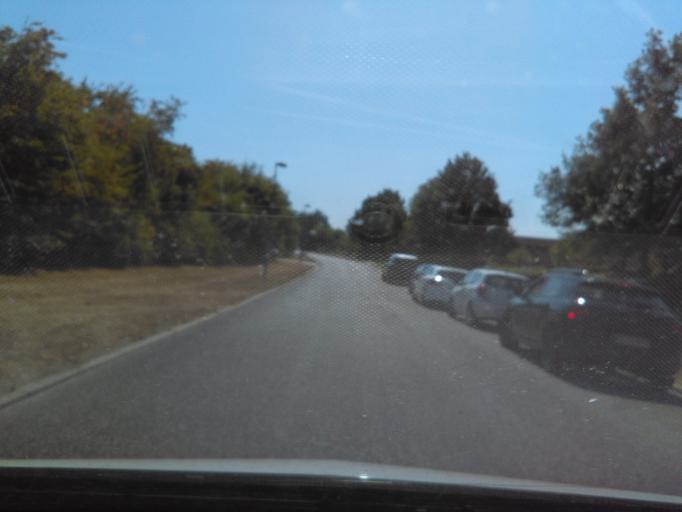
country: DK
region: Capital Region
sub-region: Fureso Kommune
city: Stavnsholt
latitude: 55.8240
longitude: 12.3864
